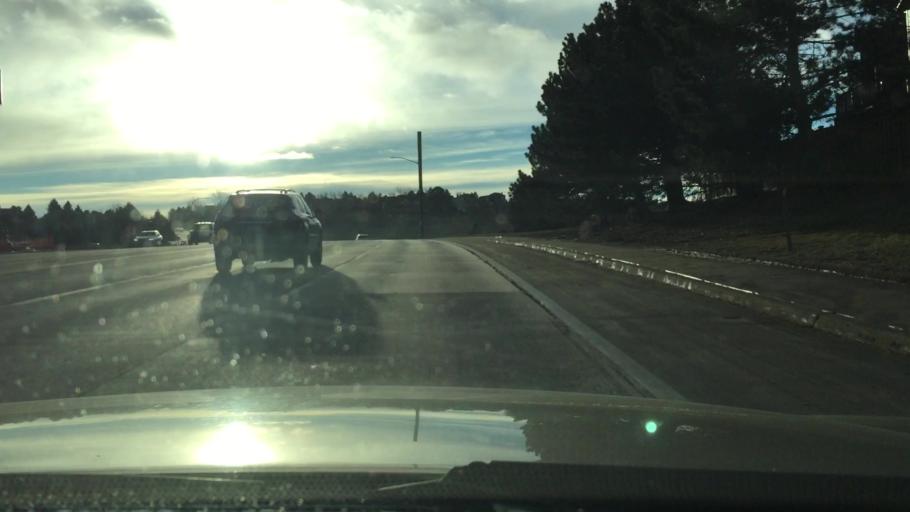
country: US
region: Colorado
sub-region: Douglas County
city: Highlands Ranch
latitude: 39.5425
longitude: -104.9689
